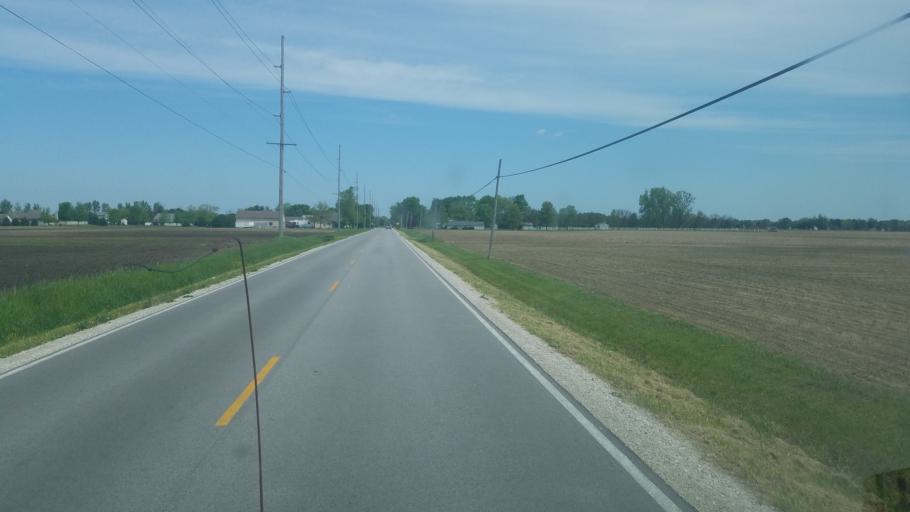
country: US
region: Ohio
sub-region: Sandusky County
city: Ballville
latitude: 41.3053
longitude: -83.1301
